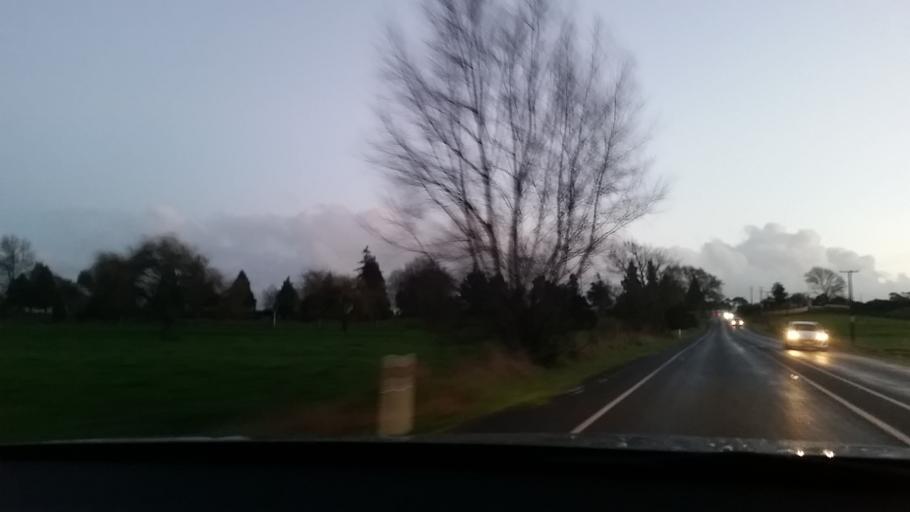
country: NZ
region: Waikato
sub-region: Hamilton City
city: Hamilton
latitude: -37.8124
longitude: 175.2339
